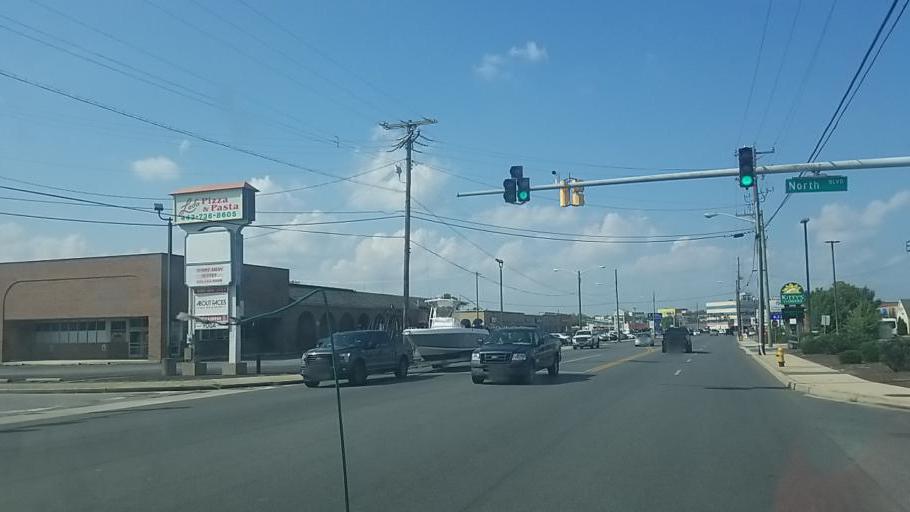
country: US
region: Maryland
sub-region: Wicomico County
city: Salisbury
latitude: 38.3555
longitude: -75.6004
